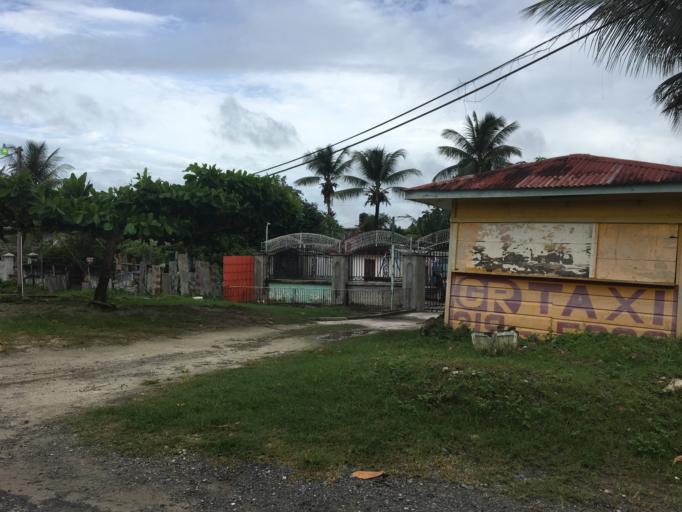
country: GY
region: Demerara-Mahaica
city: Georgetown
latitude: 6.8043
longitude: -58.1307
